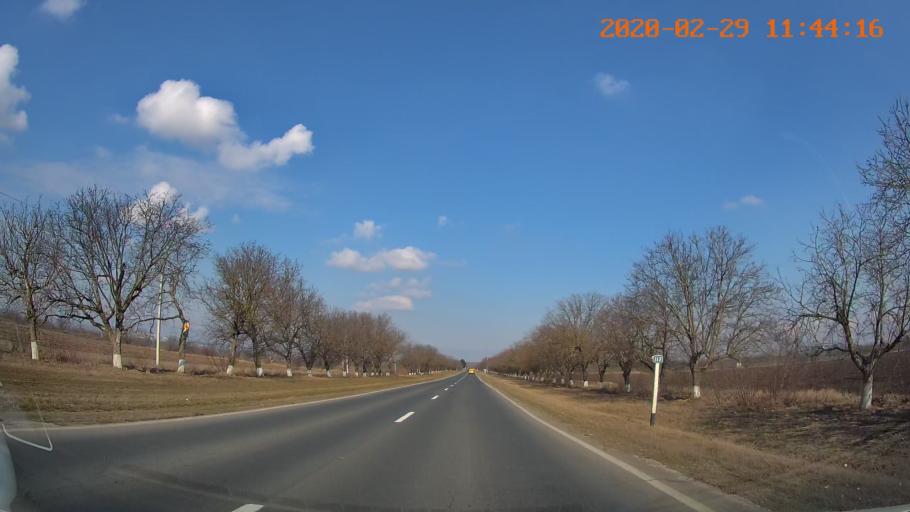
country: MD
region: Rezina
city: Saharna
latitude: 47.7089
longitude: 29.0009
